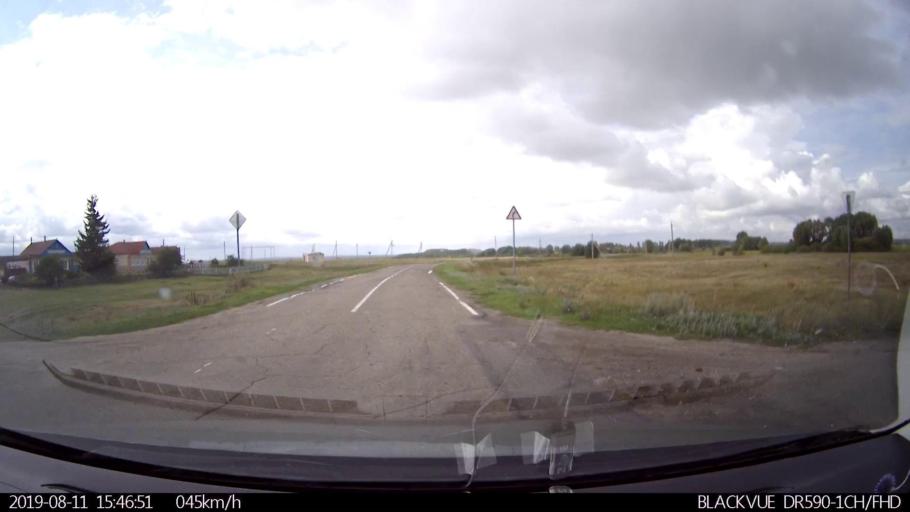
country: RU
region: Ulyanovsk
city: Ignatovka
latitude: 53.8845
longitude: 47.6539
